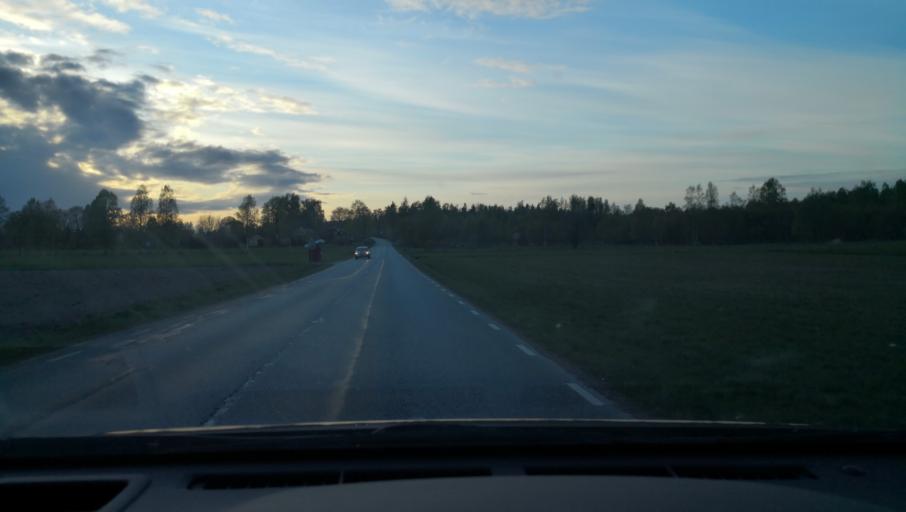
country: SE
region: OErebro
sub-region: Askersunds Kommun
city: Asbro
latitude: 58.9300
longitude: 15.0292
